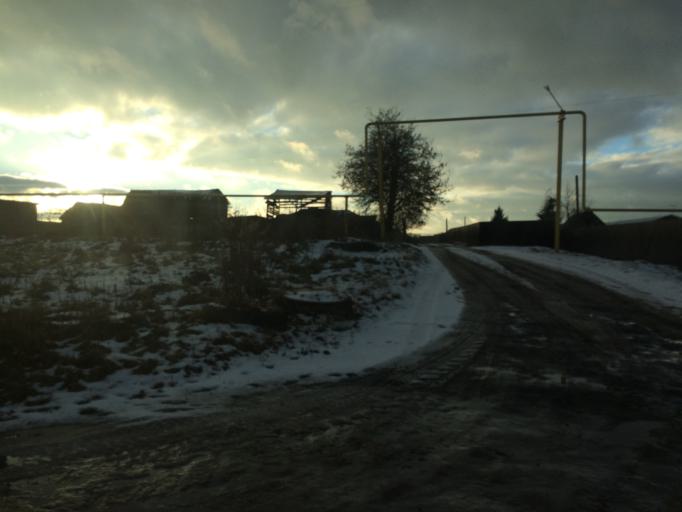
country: RU
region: Tula
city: Cherepet'
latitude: 54.1111
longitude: 36.3273
